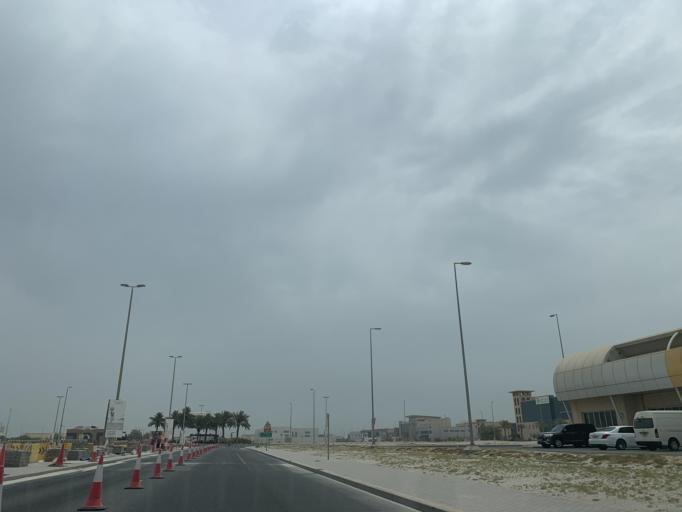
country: BH
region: Muharraq
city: Al Hadd
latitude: 26.2210
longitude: 50.6723
